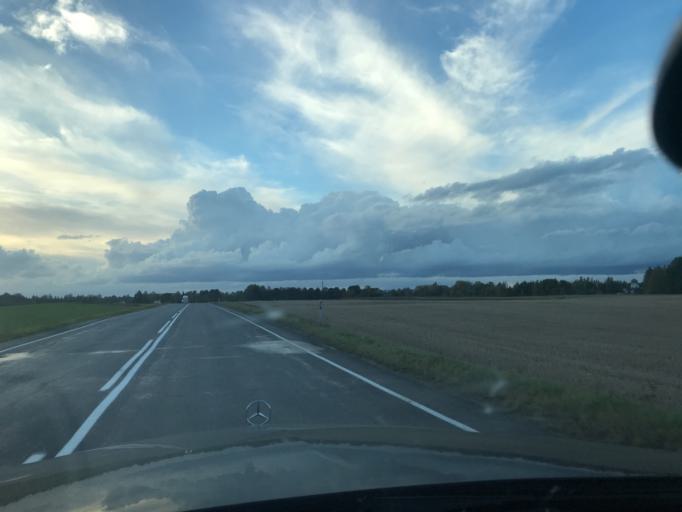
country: EE
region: Vorumaa
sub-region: Antsla vald
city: Vana-Antsla
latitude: 57.8881
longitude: 26.5142
